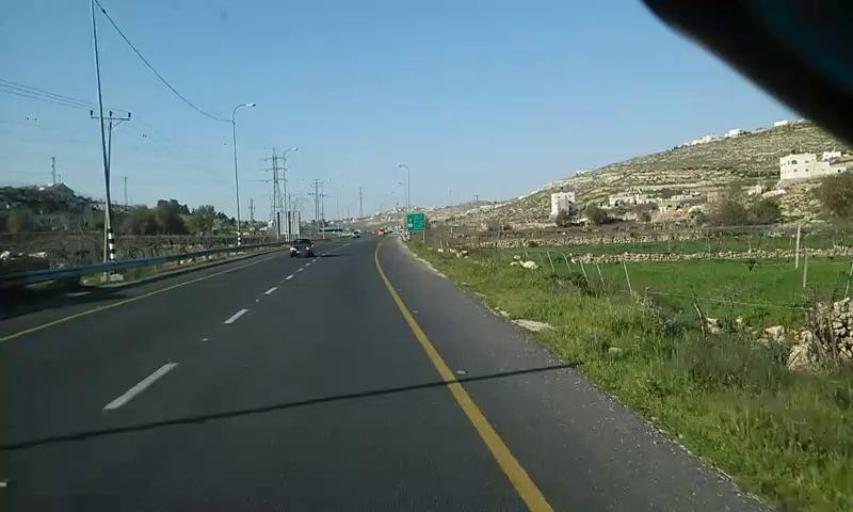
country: PS
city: Al Buq`ah
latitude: 31.5398
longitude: 35.1327
